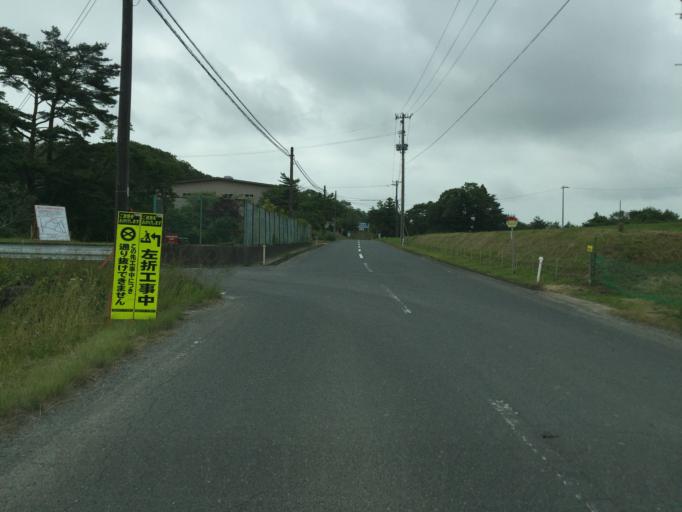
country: JP
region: Miyagi
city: Marumori
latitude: 37.7531
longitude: 140.9574
